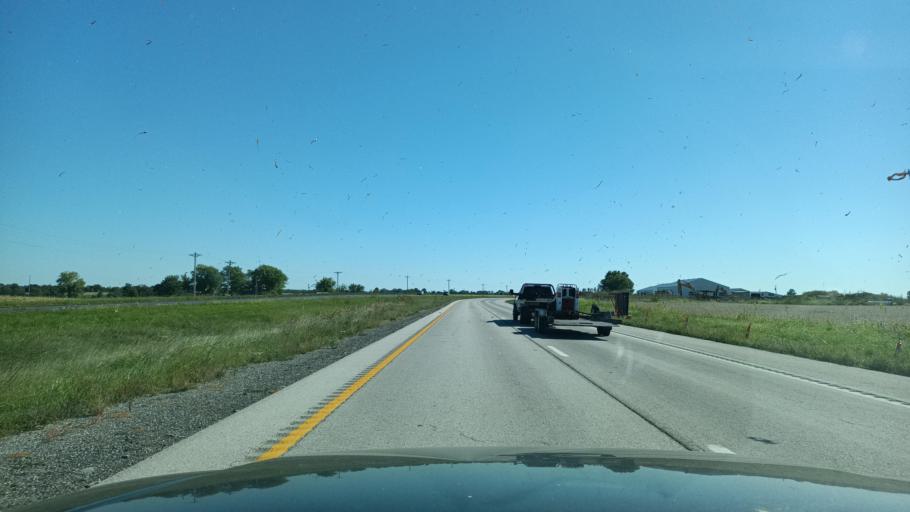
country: US
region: Missouri
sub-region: Macon County
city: Macon
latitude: 39.8207
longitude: -92.4728
